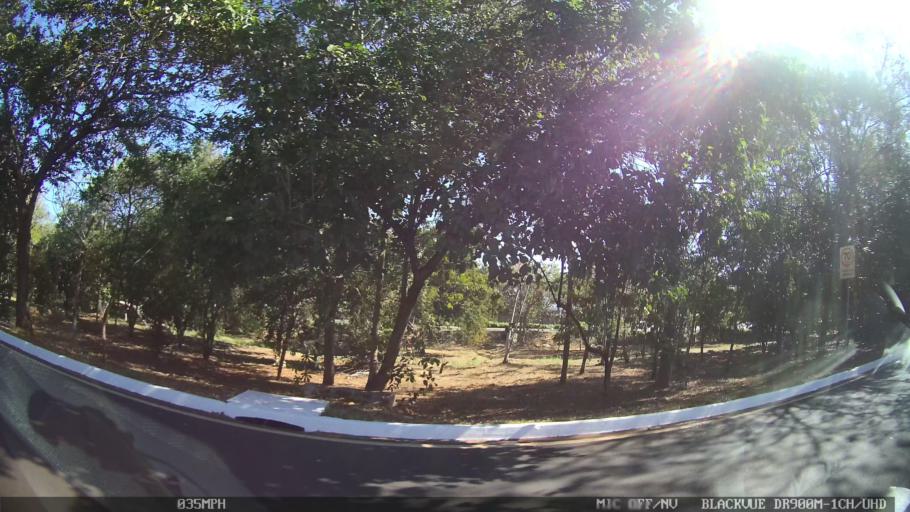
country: BR
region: Sao Paulo
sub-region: Ribeirao Preto
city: Ribeirao Preto
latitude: -21.2284
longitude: -47.7667
